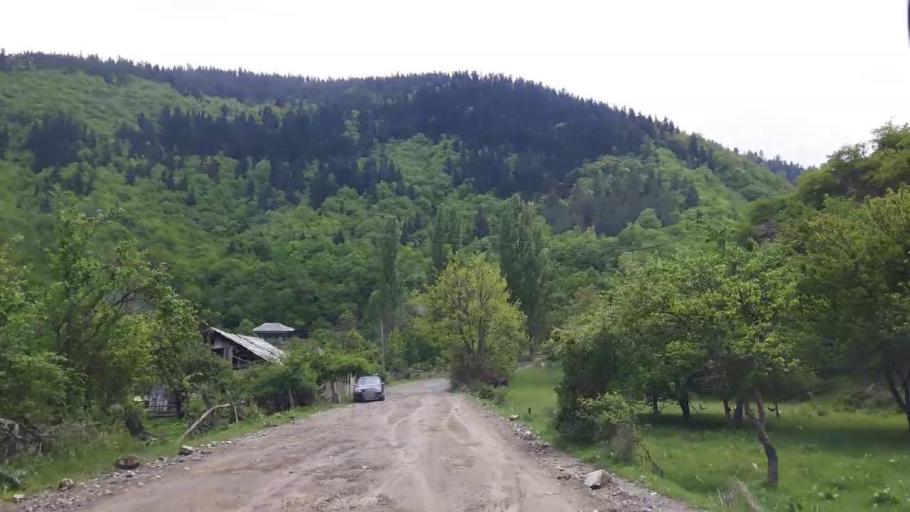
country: GE
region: Shida Kartli
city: Gori
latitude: 41.8845
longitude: 43.9977
